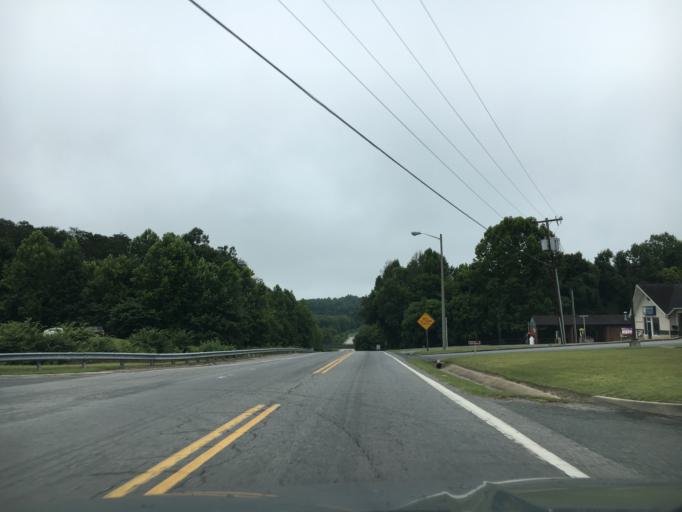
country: US
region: Virginia
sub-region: Campbell County
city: Brookneal
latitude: 37.0436
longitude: -78.9454
